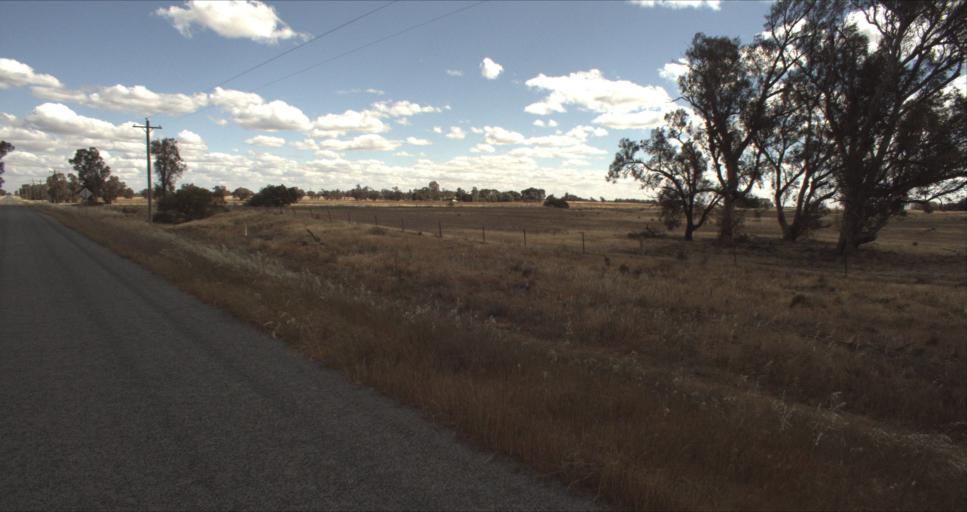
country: AU
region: New South Wales
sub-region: Leeton
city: Leeton
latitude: -34.4831
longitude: 146.2487
